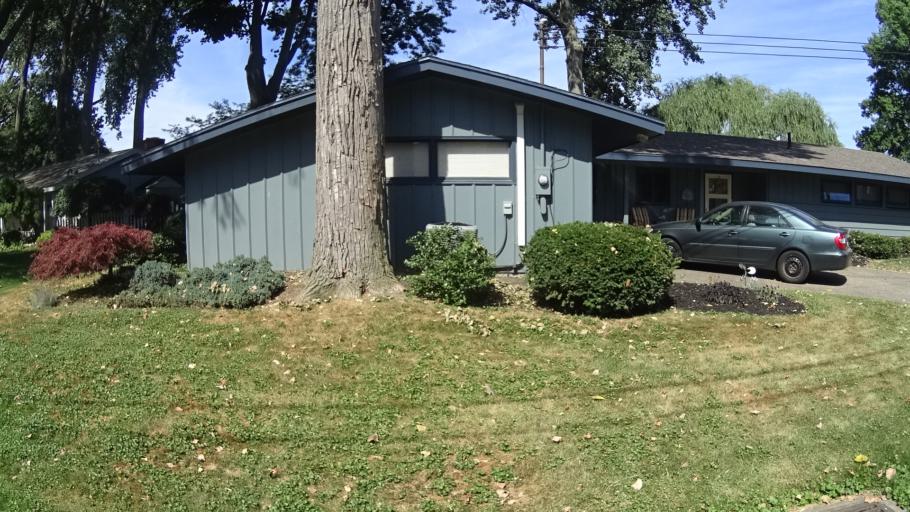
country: US
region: Ohio
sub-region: Erie County
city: Sandusky
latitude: 41.4636
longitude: -82.6640
